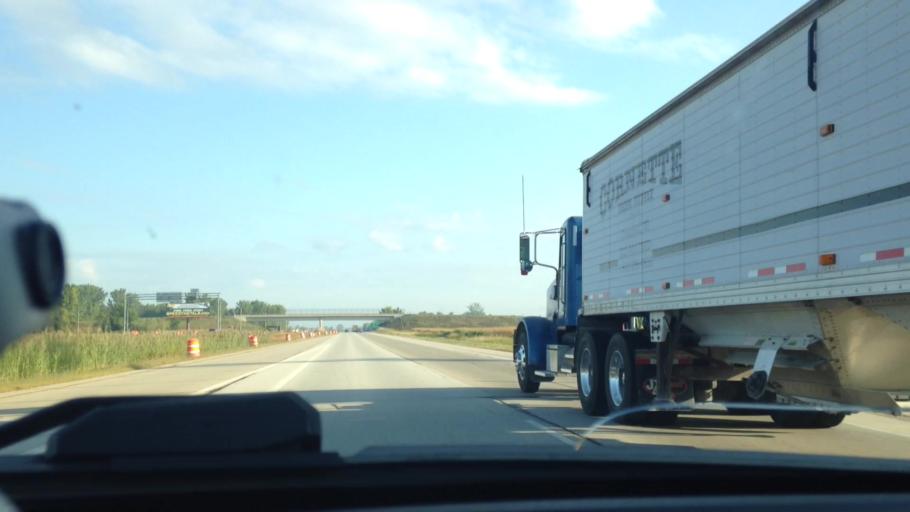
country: US
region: Wisconsin
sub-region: Brown County
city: Suamico
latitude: 44.7464
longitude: -88.0507
